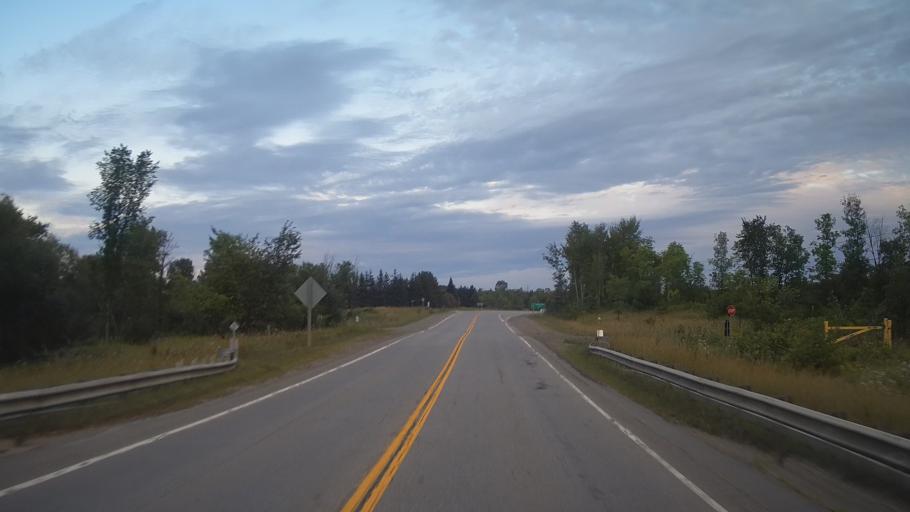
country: CA
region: Ontario
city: Pembroke
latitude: 45.7354
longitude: -76.9999
